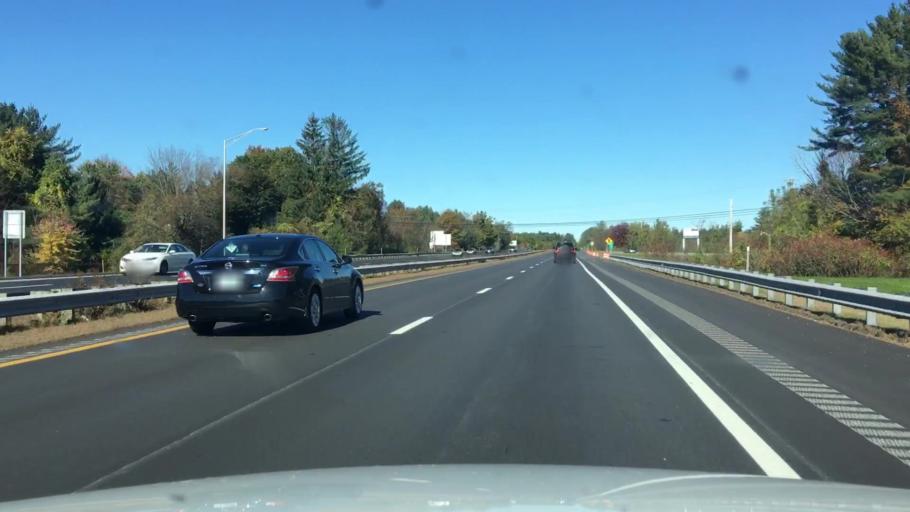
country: US
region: New Hampshire
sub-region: Strafford County
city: Dover
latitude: 43.1864
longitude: -70.8880
